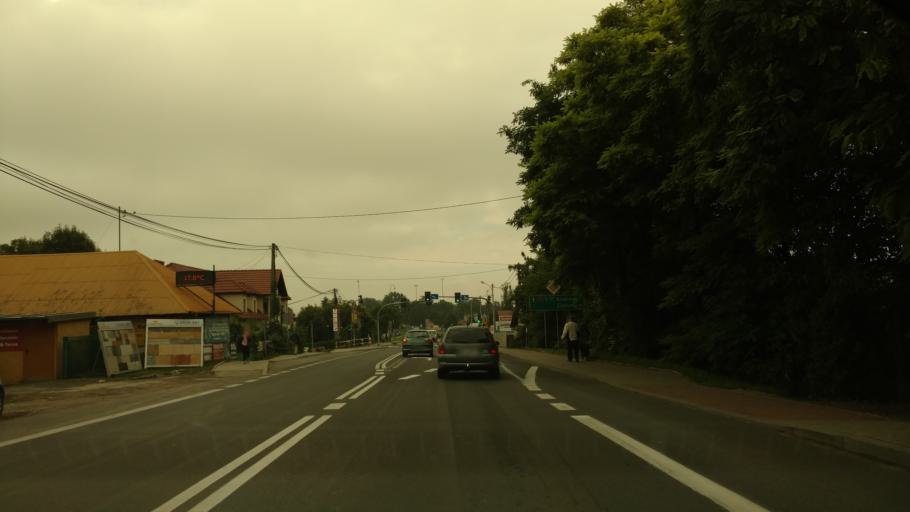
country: PL
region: Lesser Poland Voivodeship
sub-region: Powiat krakowski
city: Michalowice
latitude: 50.1210
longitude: 19.9673
